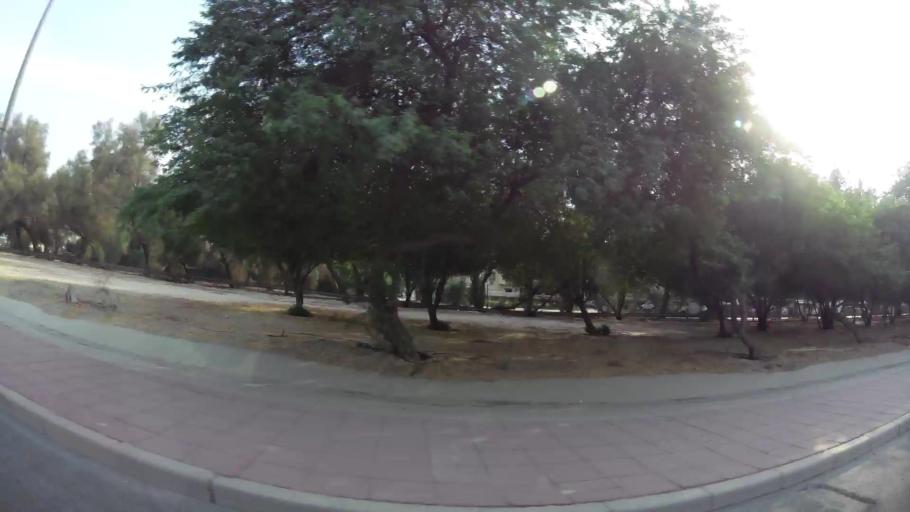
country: KW
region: Mubarak al Kabir
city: Sabah as Salim
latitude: 29.2642
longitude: 48.0555
